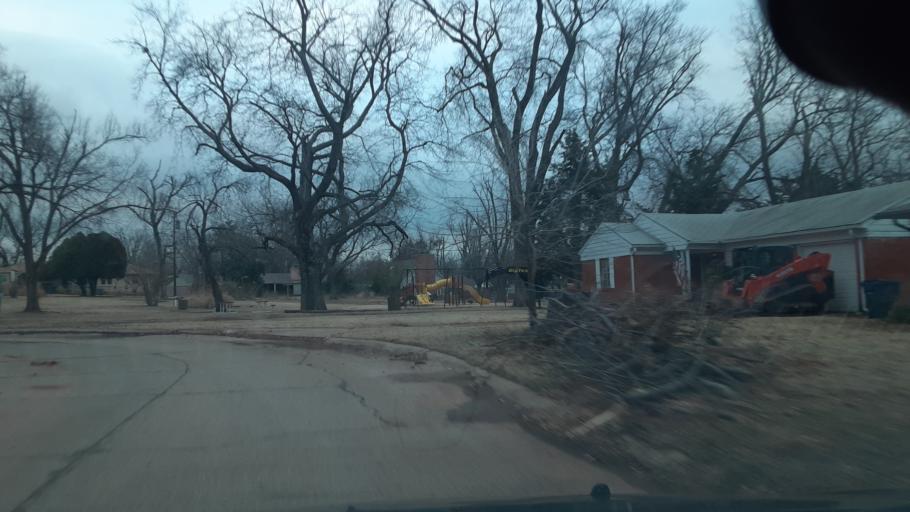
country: US
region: Oklahoma
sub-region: Logan County
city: Guthrie
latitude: 35.8900
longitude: -97.4212
